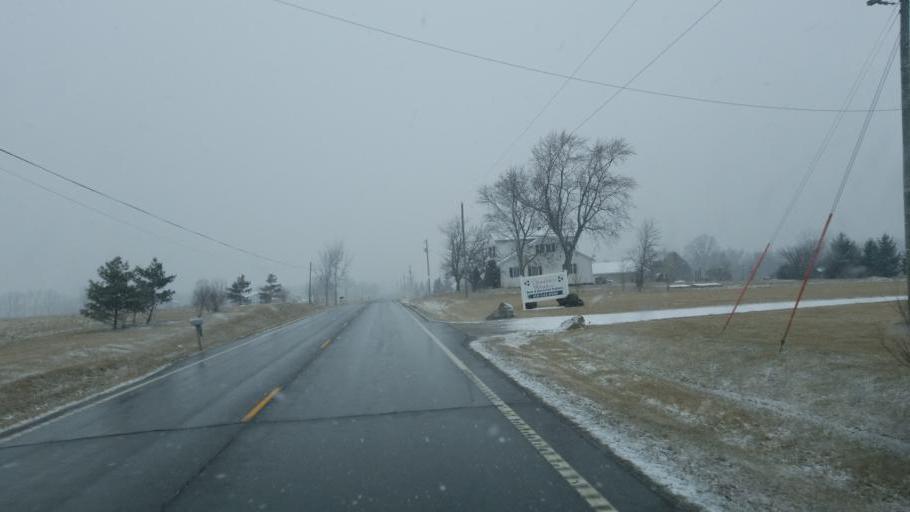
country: US
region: Ohio
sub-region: Defiance County
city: Hicksville
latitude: 41.3280
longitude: -84.7477
